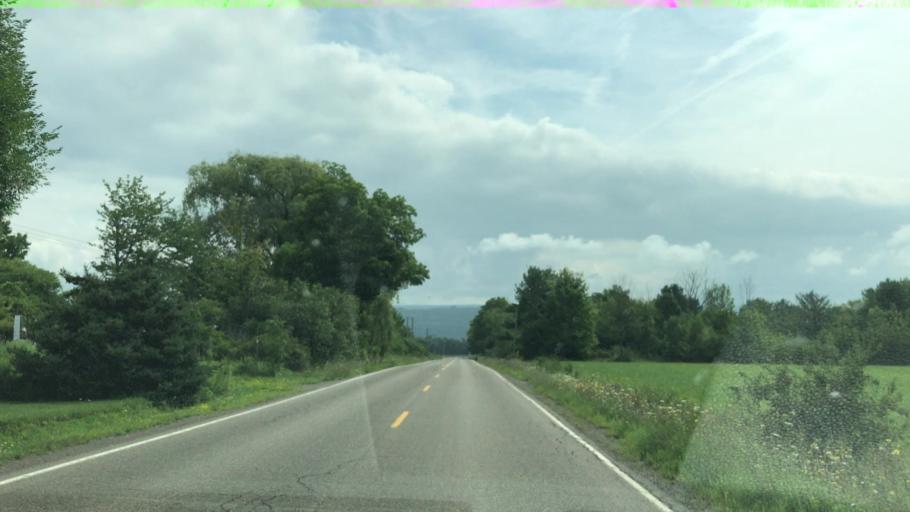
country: US
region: New York
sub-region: Steuben County
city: Sylvan Beach
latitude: 42.5127
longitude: -77.1861
